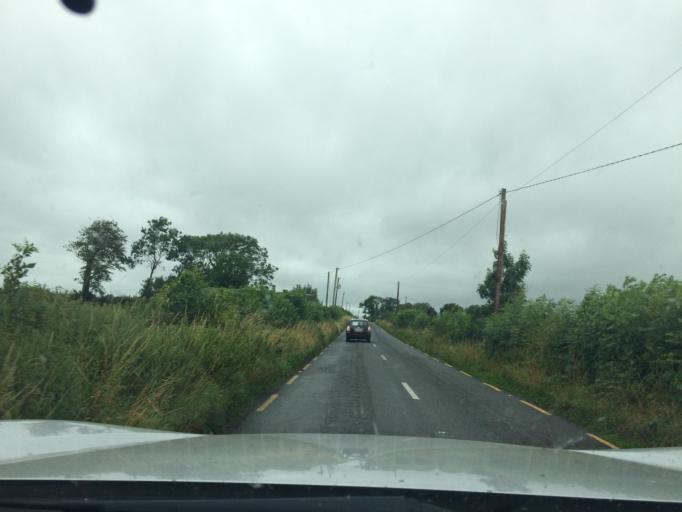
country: IE
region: Munster
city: Cashel
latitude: 52.4865
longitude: -7.8558
